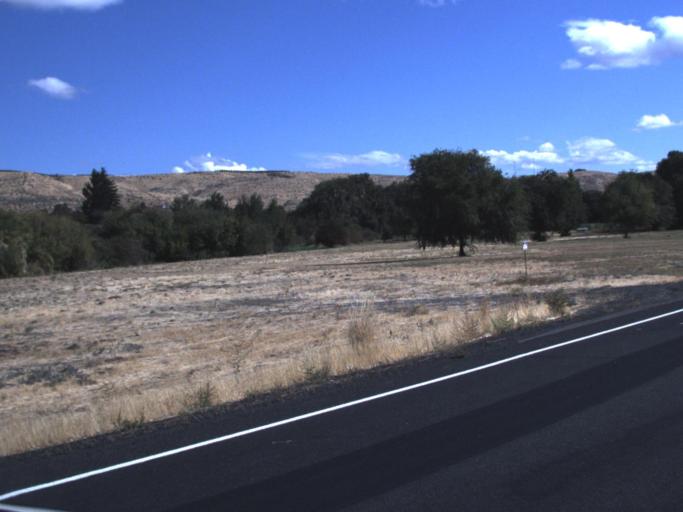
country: US
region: Washington
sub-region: Yakima County
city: Tieton
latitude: 46.7329
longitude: -120.7171
